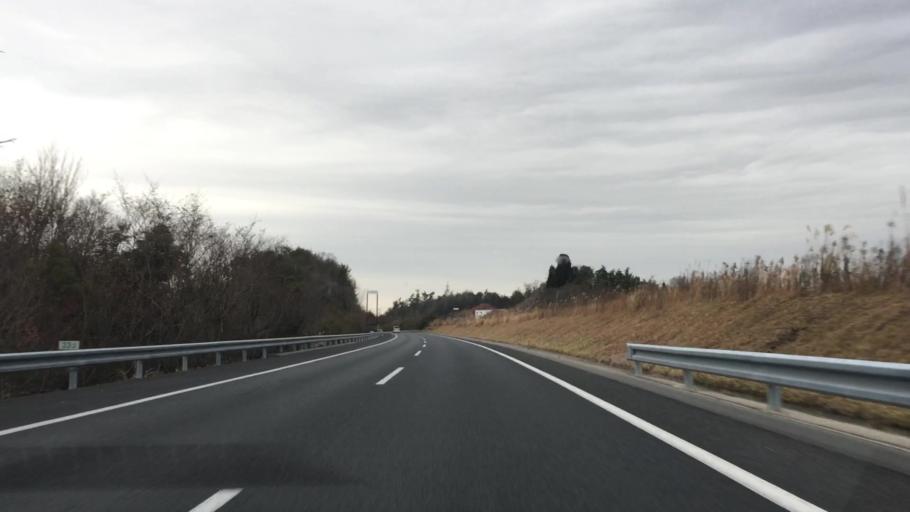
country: JP
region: Gifu
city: Toki
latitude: 35.3003
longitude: 137.1807
